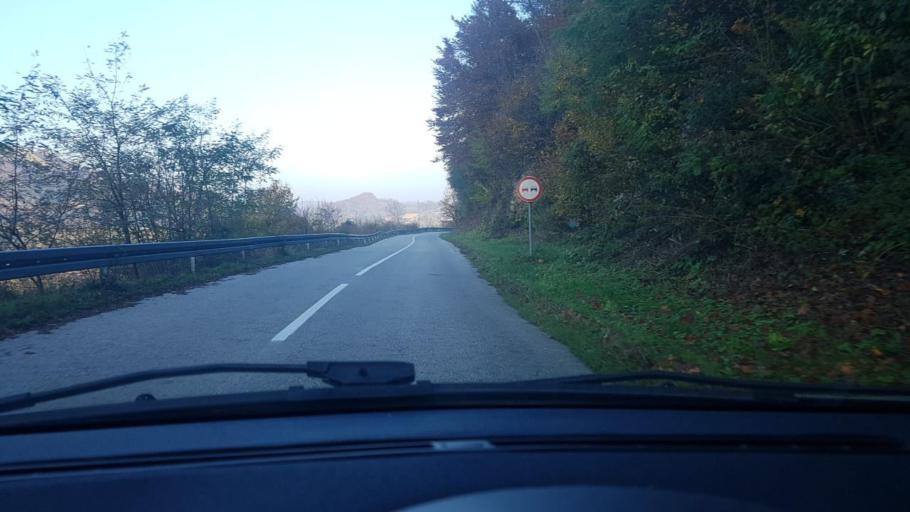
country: SI
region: Podcetrtek
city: Podcetrtek
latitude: 46.1719
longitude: 15.6228
